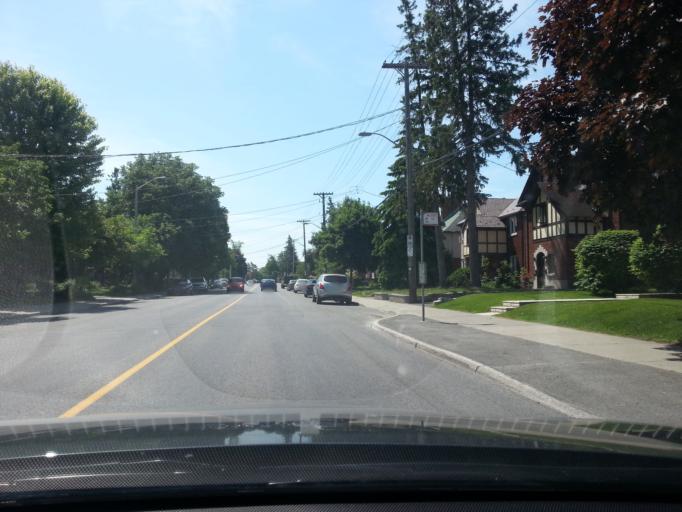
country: CA
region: Ontario
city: Ottawa
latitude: 45.3924
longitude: -75.7276
